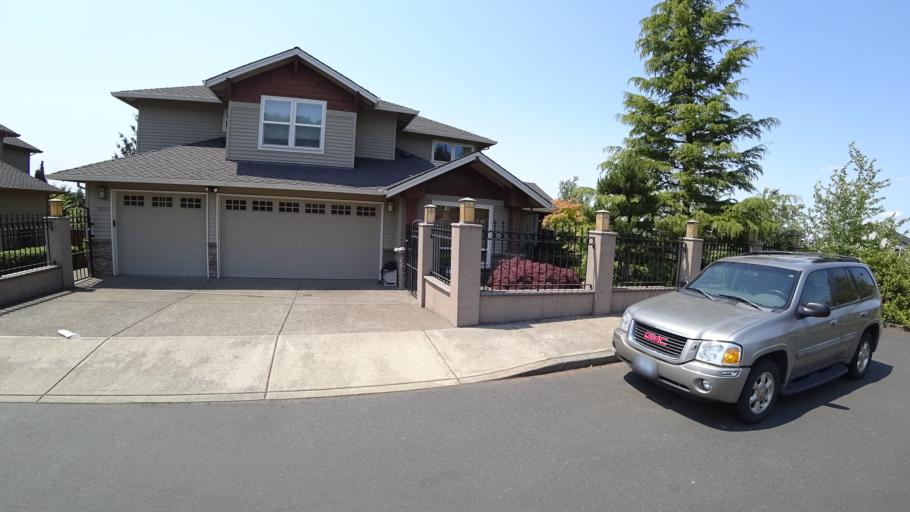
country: US
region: Oregon
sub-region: Multnomah County
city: Lents
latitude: 45.4559
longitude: -122.5590
